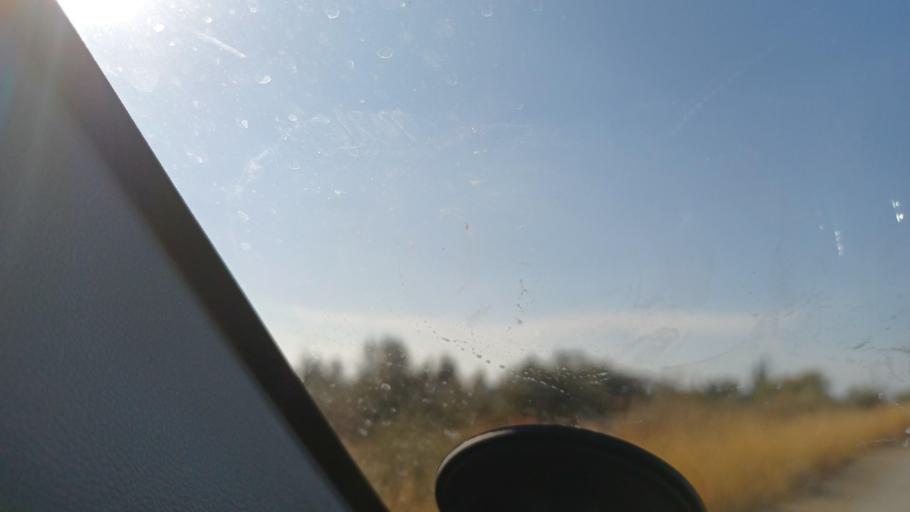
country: CY
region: Pafos
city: Mesogi
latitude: 34.7324
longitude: 32.5459
